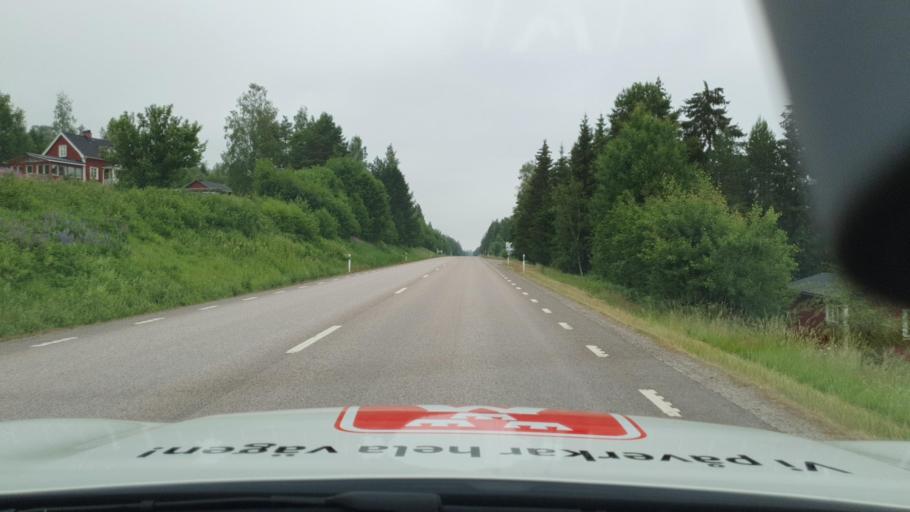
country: SE
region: Vaermland
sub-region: Sunne Kommun
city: Sunne
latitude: 59.8831
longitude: 13.1403
